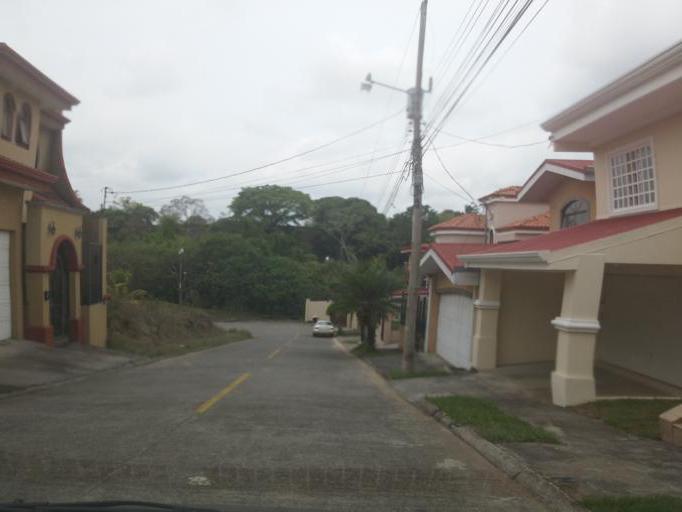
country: CR
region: Alajuela
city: Alajuela
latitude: 10.0275
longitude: -84.2118
